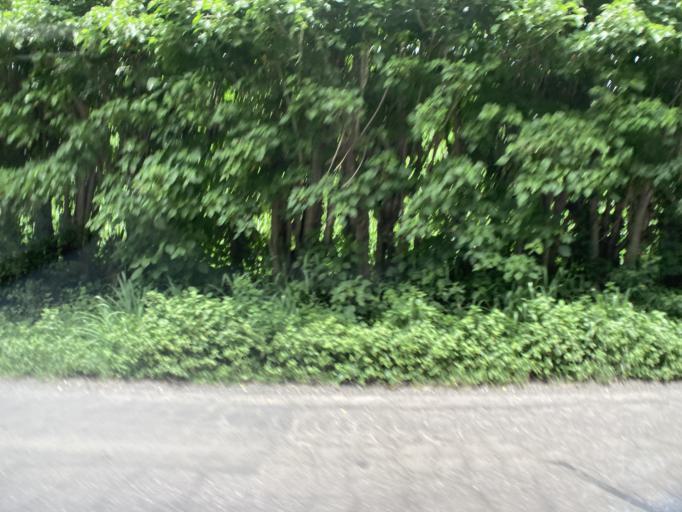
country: GT
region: Guatemala
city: Villa Canales
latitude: 14.4298
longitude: -90.5583
